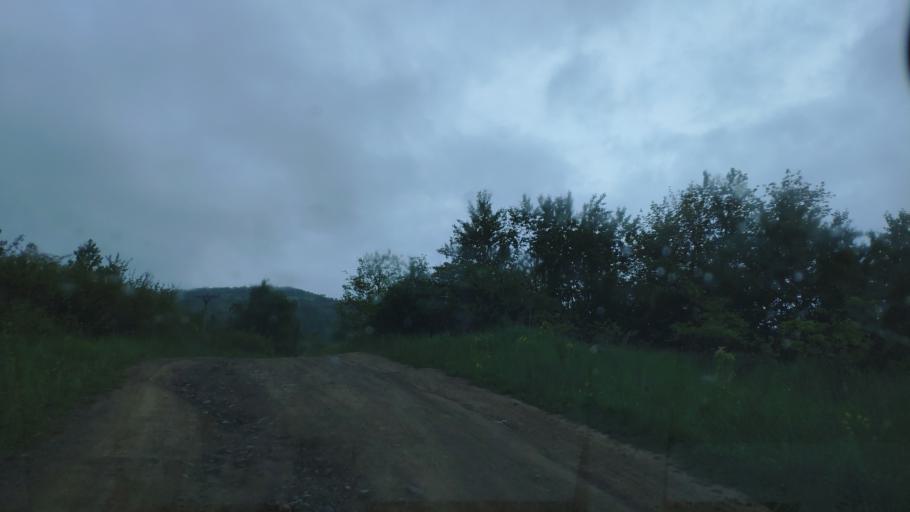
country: SK
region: Kosicky
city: Kosice
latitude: 48.7631
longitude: 21.2024
